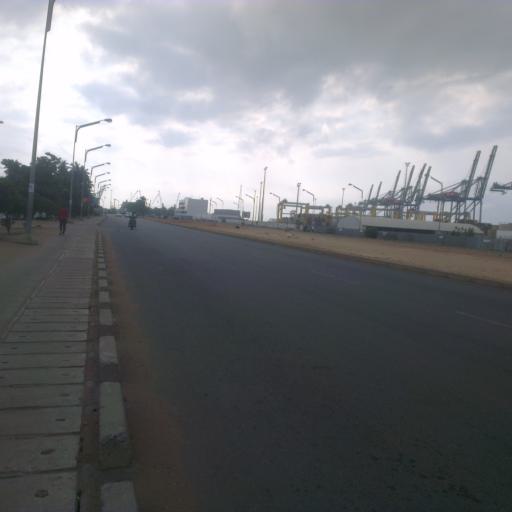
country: TG
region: Maritime
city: Lome
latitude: 6.1393
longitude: 1.2703
